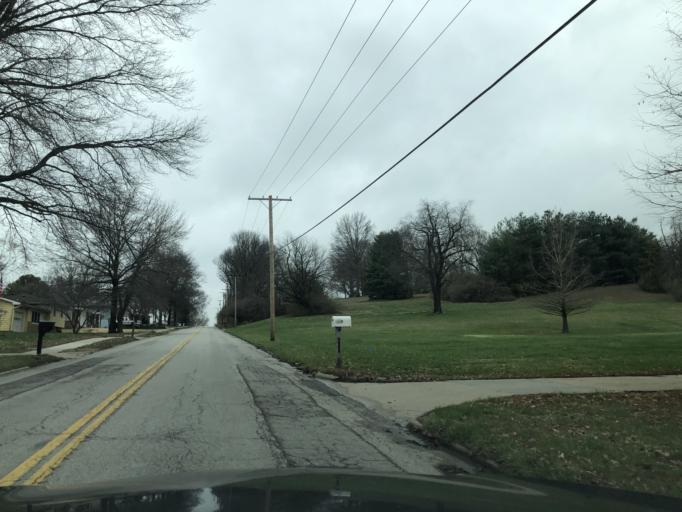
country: US
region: Kansas
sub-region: Leavenworth County
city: Leavenworth
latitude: 39.2784
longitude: -94.9185
